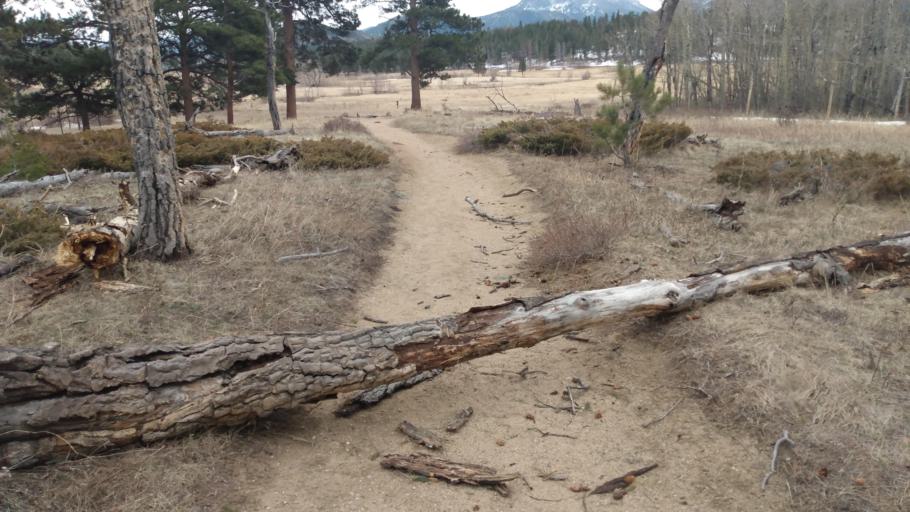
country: US
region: Colorado
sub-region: Larimer County
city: Estes Park
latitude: 40.3731
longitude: -105.6154
